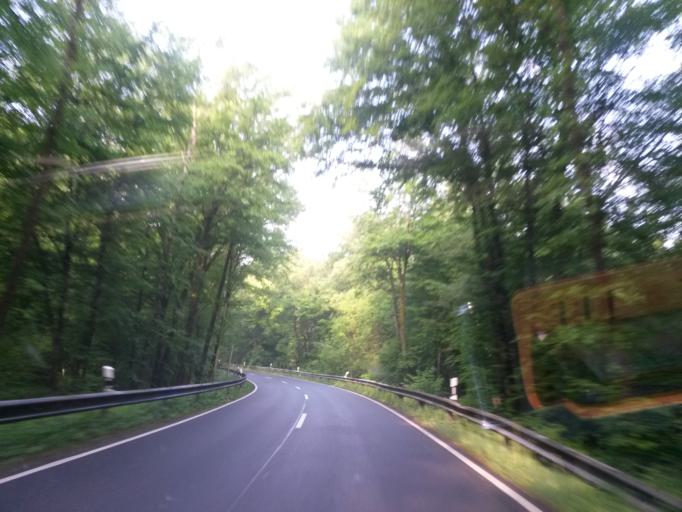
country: DE
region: North Rhine-Westphalia
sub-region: Regierungsbezirk Koln
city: Much
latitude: 50.8816
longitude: 7.3619
